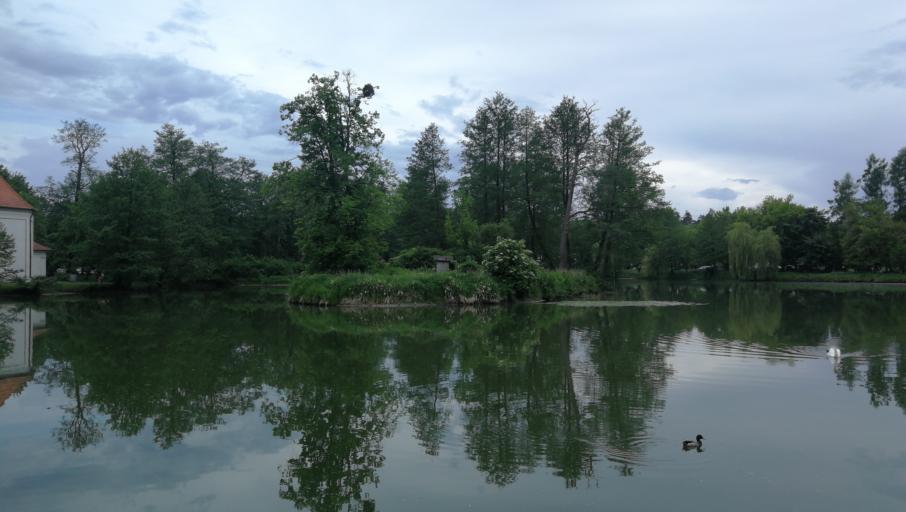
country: PL
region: Lublin Voivodeship
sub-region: Powiat zamojski
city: Zwierzyniec
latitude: 50.6101
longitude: 22.9674
